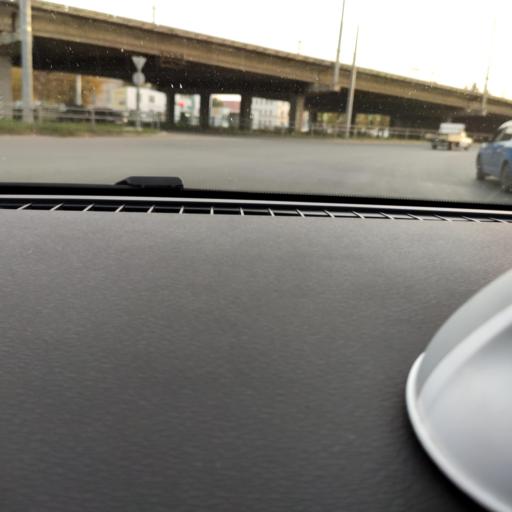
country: RU
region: Samara
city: Smyshlyayevka
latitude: 53.2076
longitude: 50.2762
